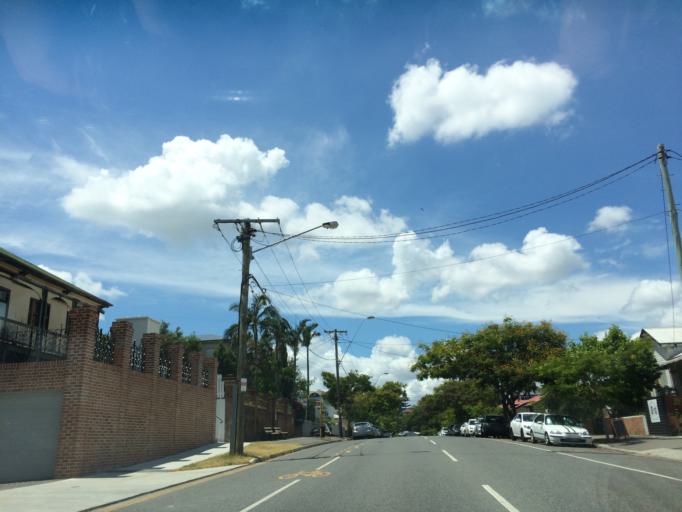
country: AU
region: Queensland
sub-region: Brisbane
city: South Brisbane
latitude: -27.4790
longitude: 153.0140
